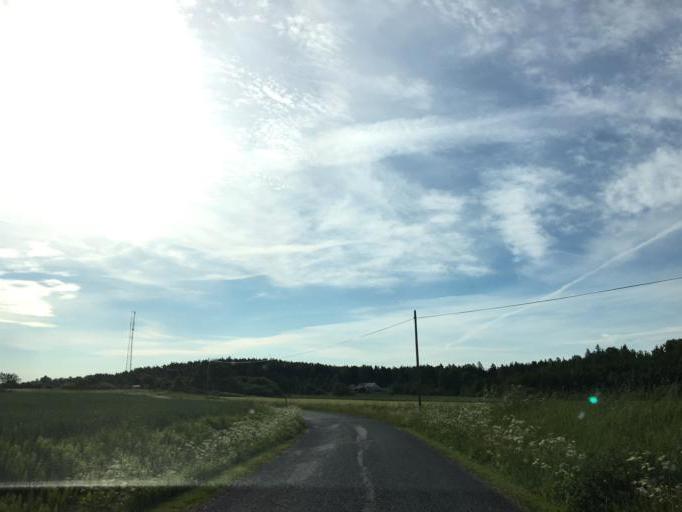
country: SE
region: Soedermanland
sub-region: Eskilstuna Kommun
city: Hallbybrunn
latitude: 59.4297
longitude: 16.3979
